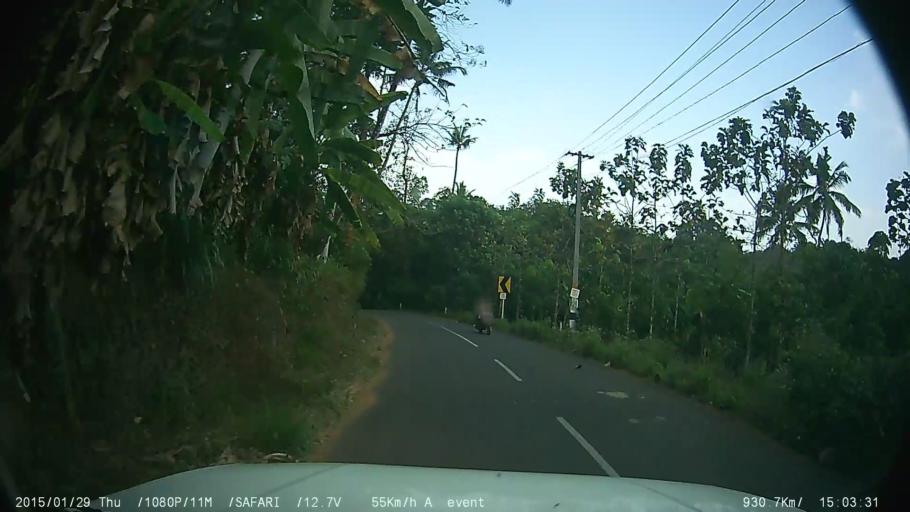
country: IN
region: Kerala
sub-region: Kottayam
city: Palackattumala
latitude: 9.7268
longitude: 76.5823
